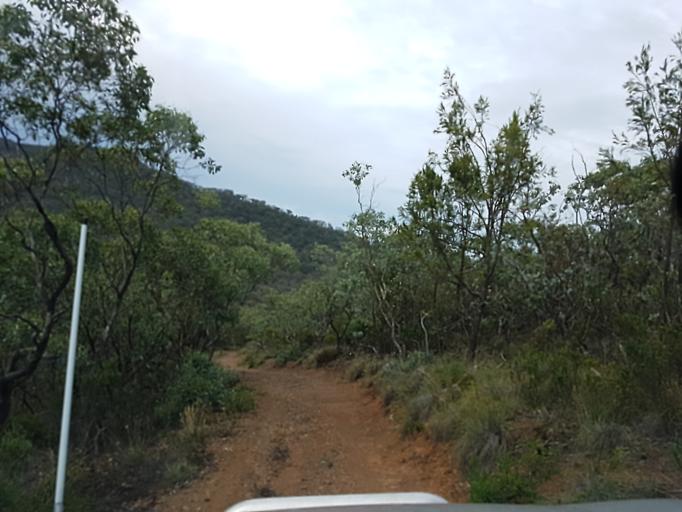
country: AU
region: New South Wales
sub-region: Snowy River
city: Jindabyne
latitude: -36.9964
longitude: 148.4058
